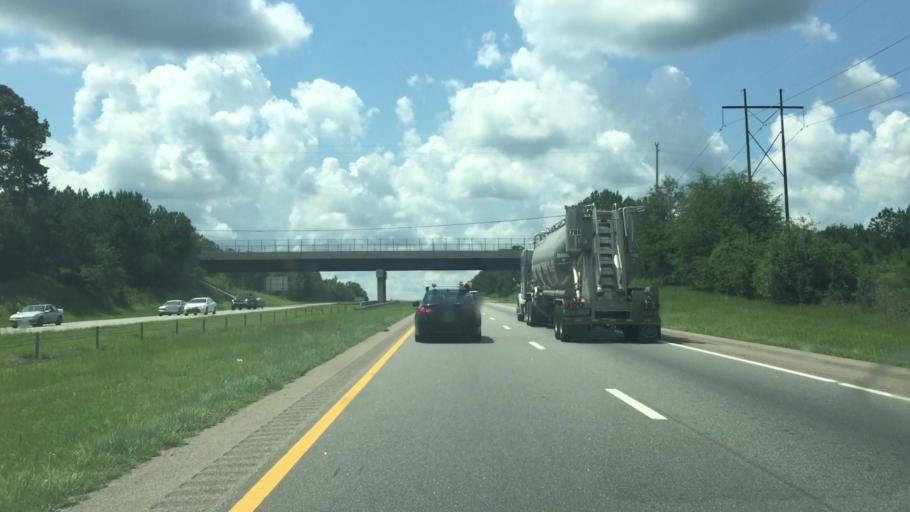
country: US
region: North Carolina
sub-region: Richmond County
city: East Rockingham
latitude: 34.9002
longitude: -79.7907
